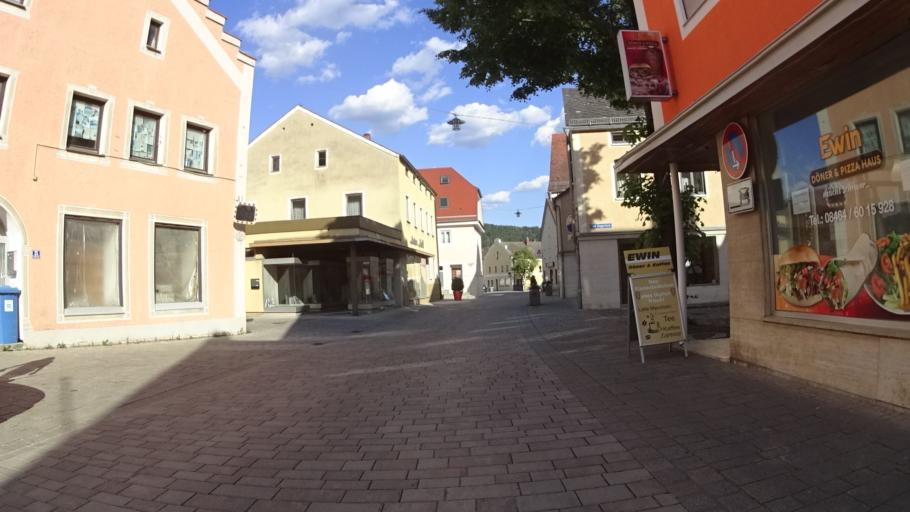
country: DE
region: Bavaria
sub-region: Upper Palatinate
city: Dietfurt
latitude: 49.0346
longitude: 11.5890
